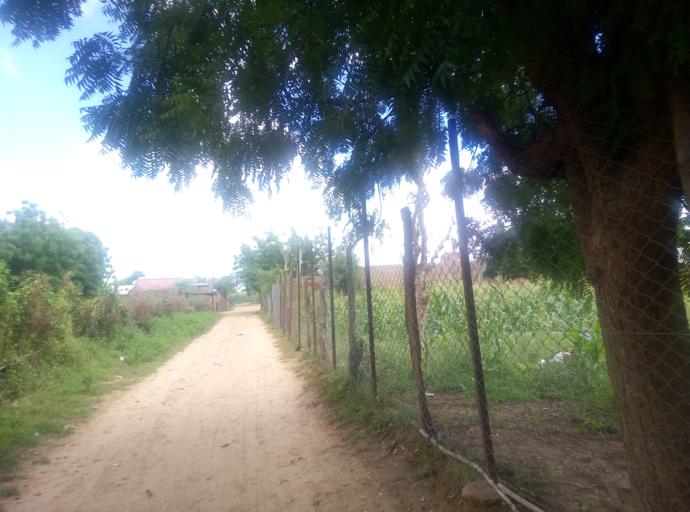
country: ML
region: Kayes
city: Yelimane
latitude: 15.1243
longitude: -10.7293
